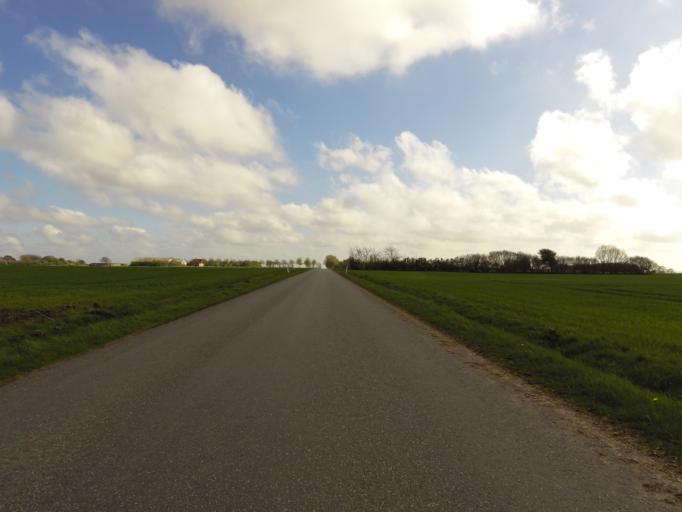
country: DK
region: South Denmark
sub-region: Haderslev Kommune
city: Gram
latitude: 55.3317
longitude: 8.9836
